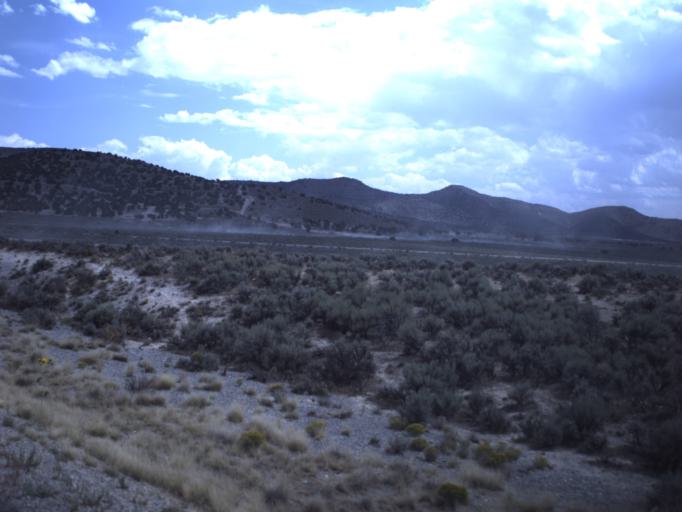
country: US
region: Utah
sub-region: Utah County
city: Eagle Mountain
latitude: 40.2313
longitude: -112.1880
